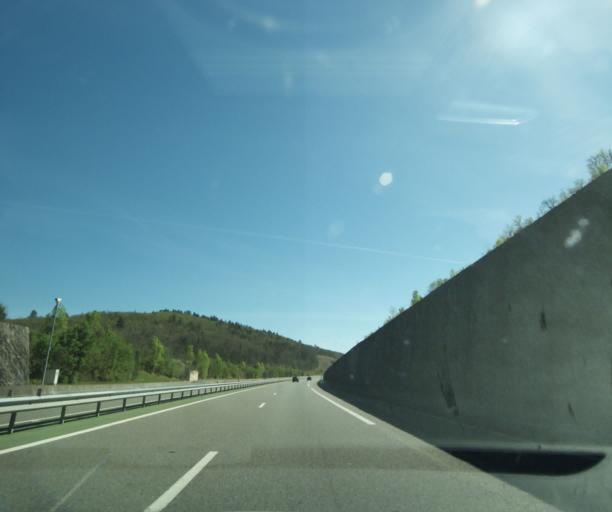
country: FR
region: Midi-Pyrenees
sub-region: Departement du Lot
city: Cahors
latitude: 44.4537
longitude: 1.5052
